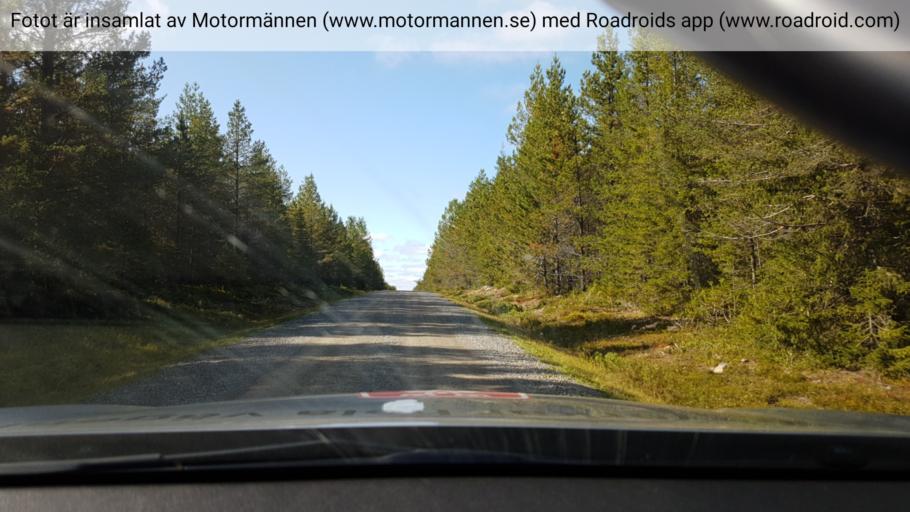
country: SE
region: Vaesterbotten
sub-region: Mala Kommun
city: Mala
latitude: 65.2119
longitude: 19.0879
